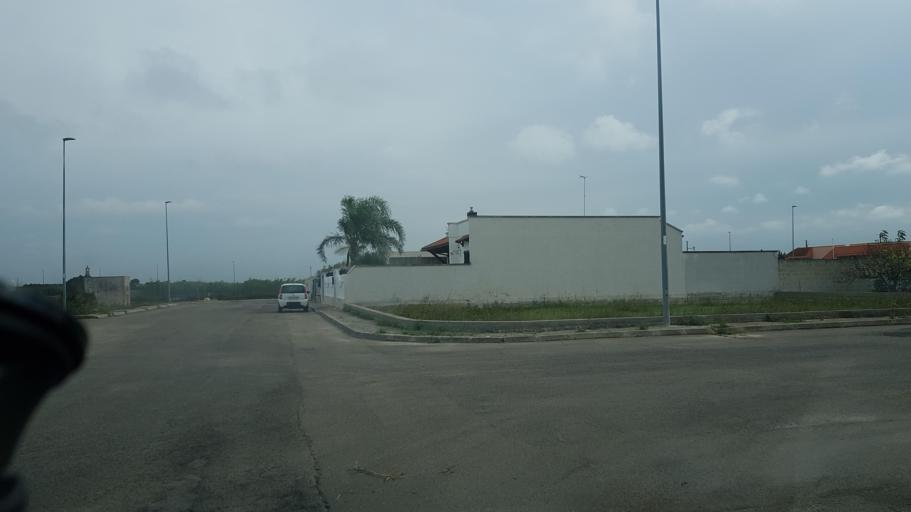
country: IT
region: Apulia
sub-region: Provincia di Lecce
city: Guagnano
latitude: 40.4062
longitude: 17.9513
